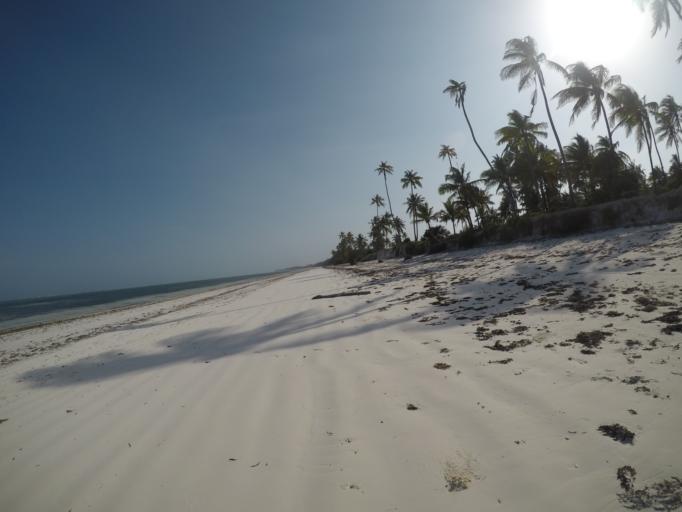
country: TZ
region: Zanzibar Central/South
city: Nganane
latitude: -6.2097
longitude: 39.5344
